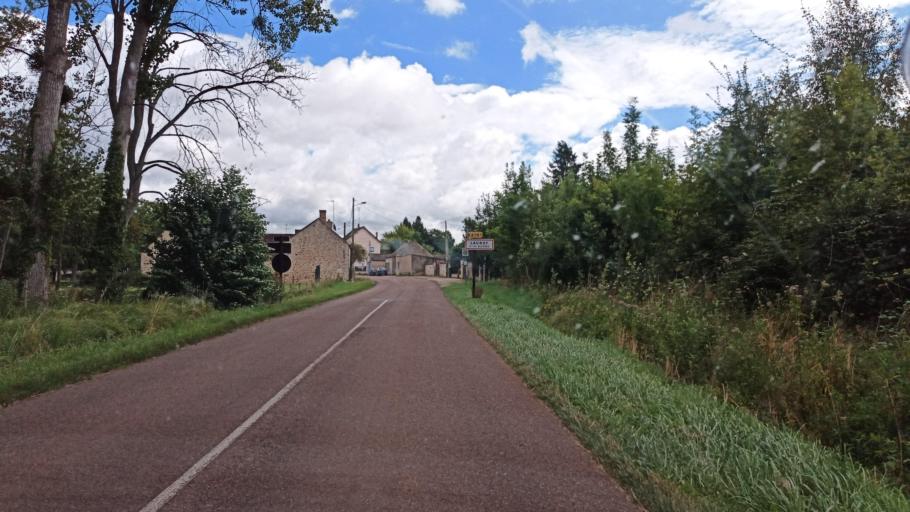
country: FR
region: Ile-de-France
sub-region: Departement de Seine-et-Marne
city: Voulx
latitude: 48.2675
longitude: 3.0024
